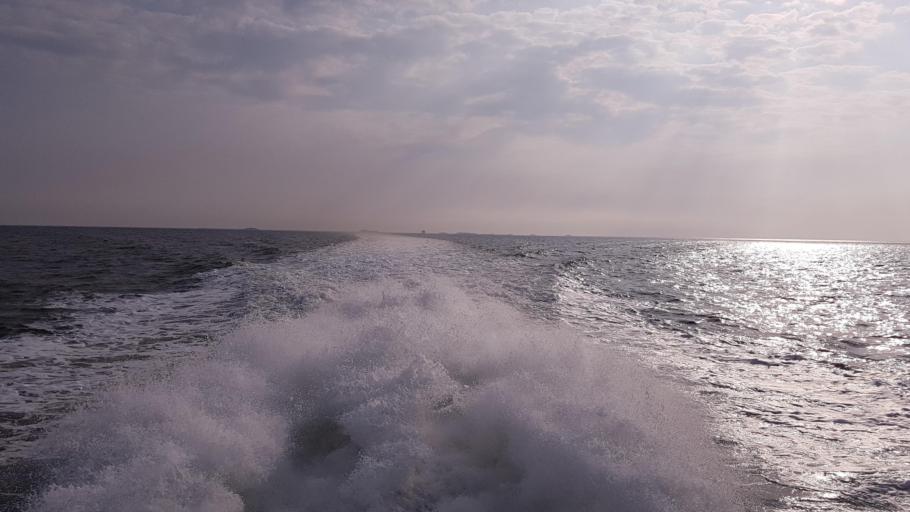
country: DE
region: Schleswig-Holstein
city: Langeness
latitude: 54.5978
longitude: 8.6403
